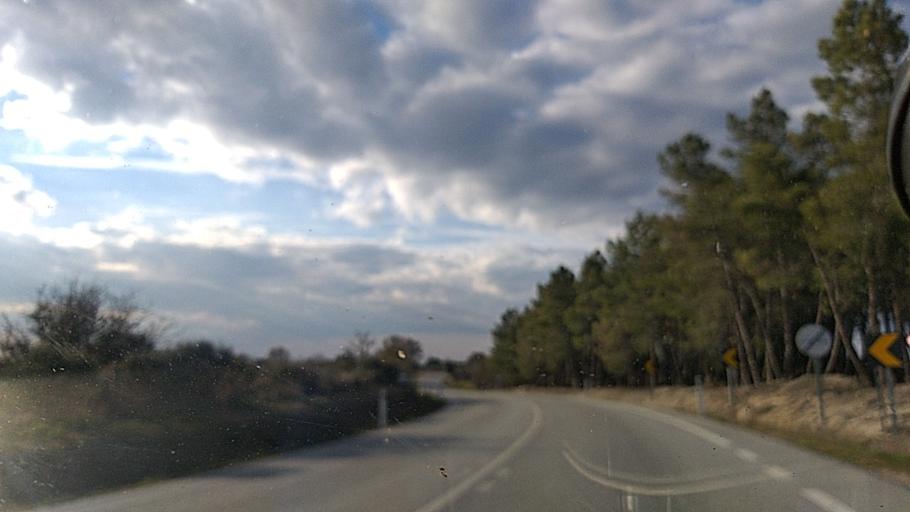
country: ES
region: Castille and Leon
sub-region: Provincia de Salamanca
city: Aldea del Obispo
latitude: 40.6836
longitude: -6.8706
